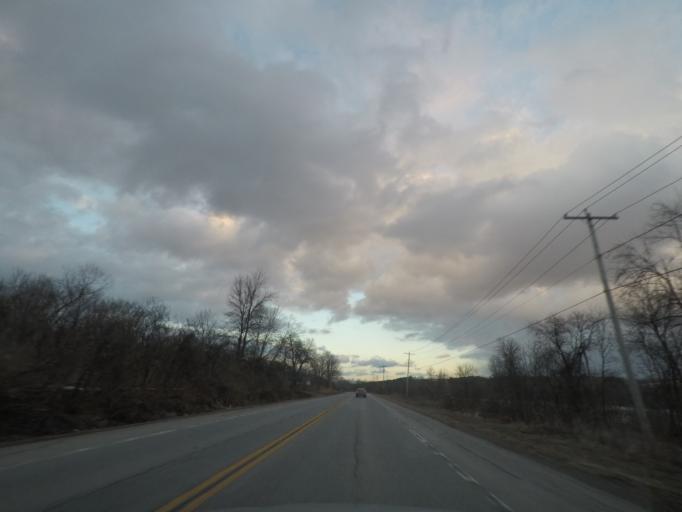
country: US
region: New York
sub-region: Montgomery County
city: Fonda
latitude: 42.9277
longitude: -74.4315
